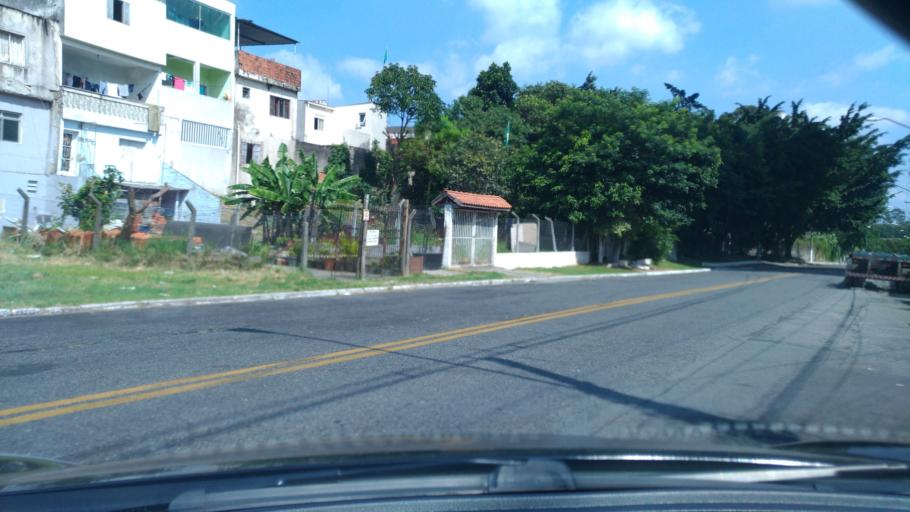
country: BR
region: Sao Paulo
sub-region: Sao Bernardo Do Campo
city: Sao Bernardo do Campo
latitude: -23.6989
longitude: -46.5830
